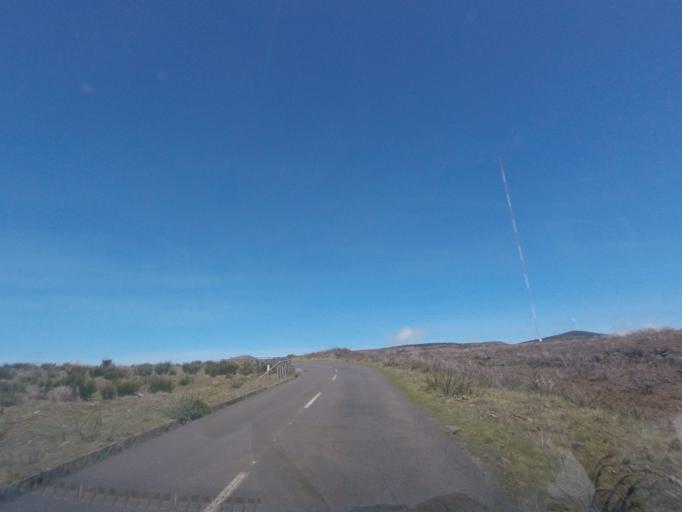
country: PT
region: Madeira
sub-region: Calheta
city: Arco da Calheta
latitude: 32.7415
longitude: -17.0974
